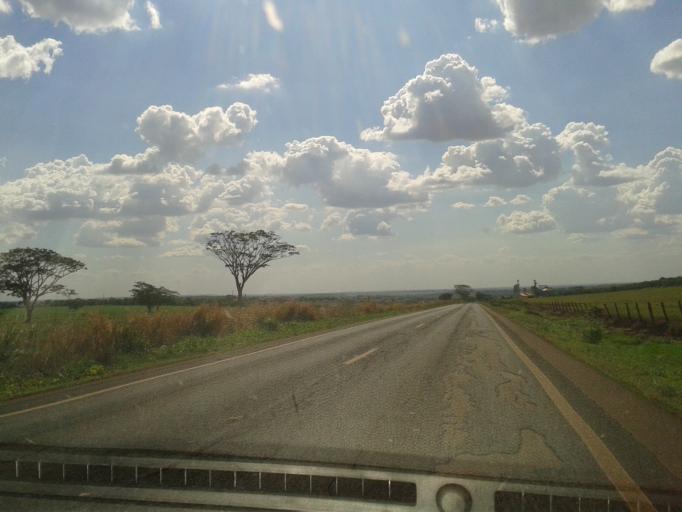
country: BR
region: Minas Gerais
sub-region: Capinopolis
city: Capinopolis
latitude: -18.6830
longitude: -49.5399
